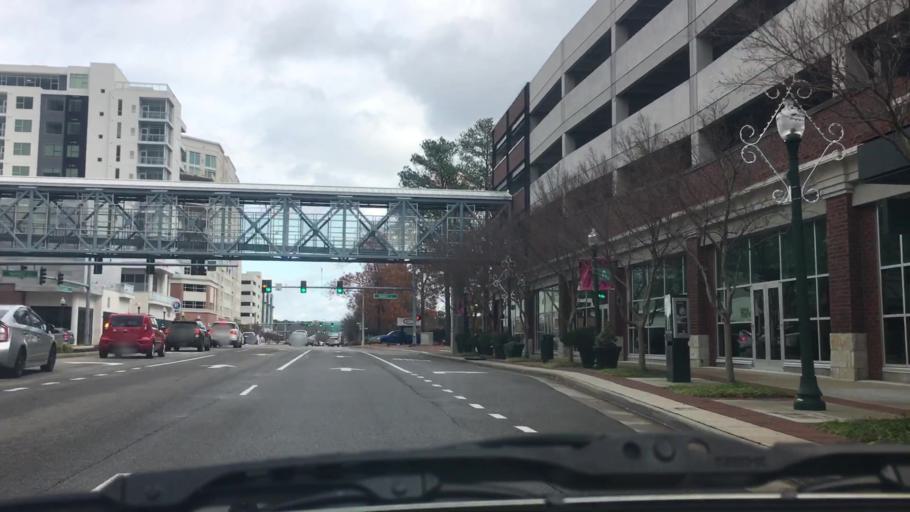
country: US
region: Virginia
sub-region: City of Chesapeake
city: Chesapeake
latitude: 36.8409
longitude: -76.1357
